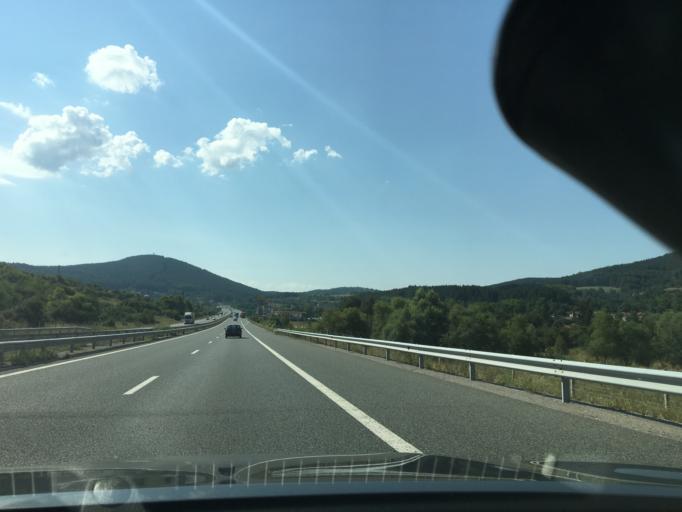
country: BG
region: Pernik
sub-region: Obshtina Pernik
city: Pernik
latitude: 42.5446
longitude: 23.1276
